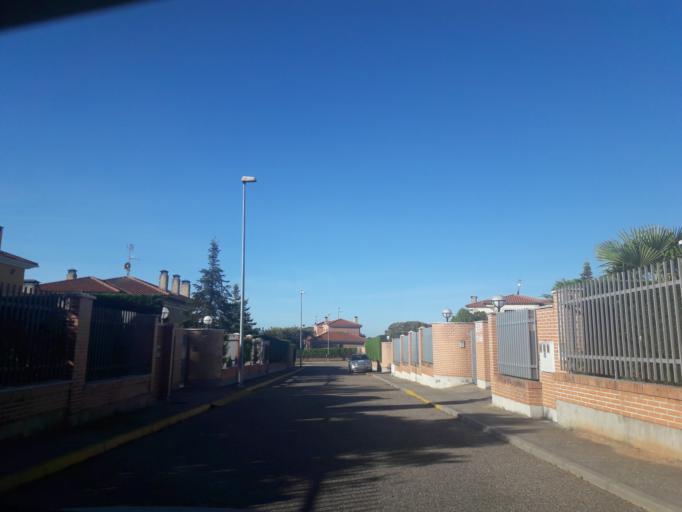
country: ES
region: Castille and Leon
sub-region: Provincia de Salamanca
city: Martinamor
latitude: 40.8087
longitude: -5.6333
